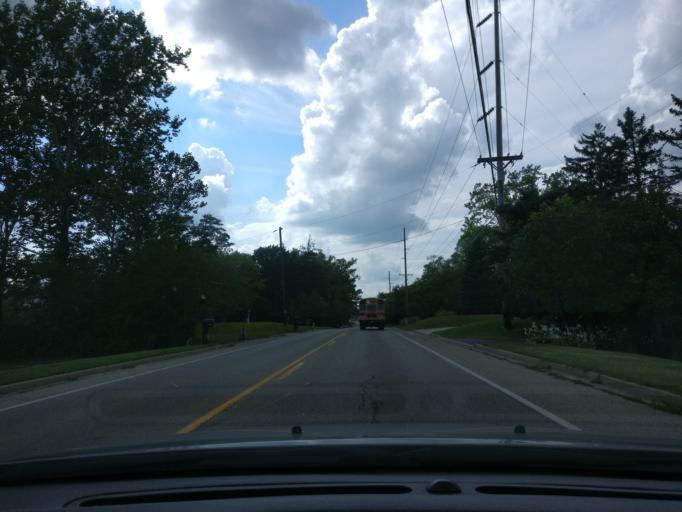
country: US
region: Ohio
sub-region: Montgomery County
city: Centerville
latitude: 39.5904
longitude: -84.1574
